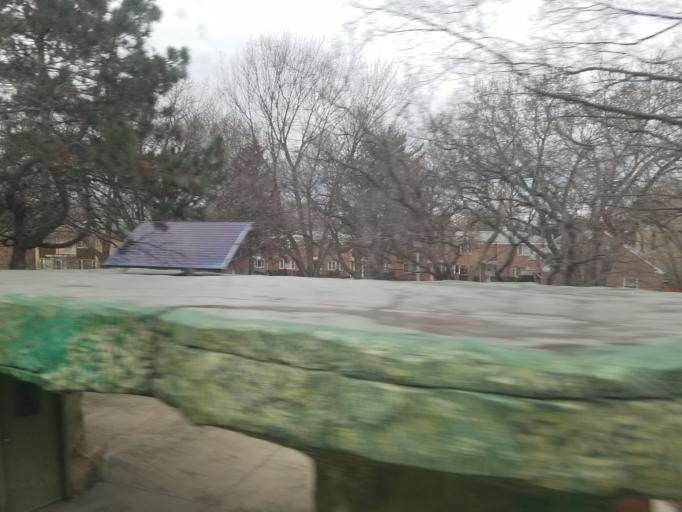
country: US
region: Illinois
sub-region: Cook County
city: Riverside
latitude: 41.8247
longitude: -87.8323
